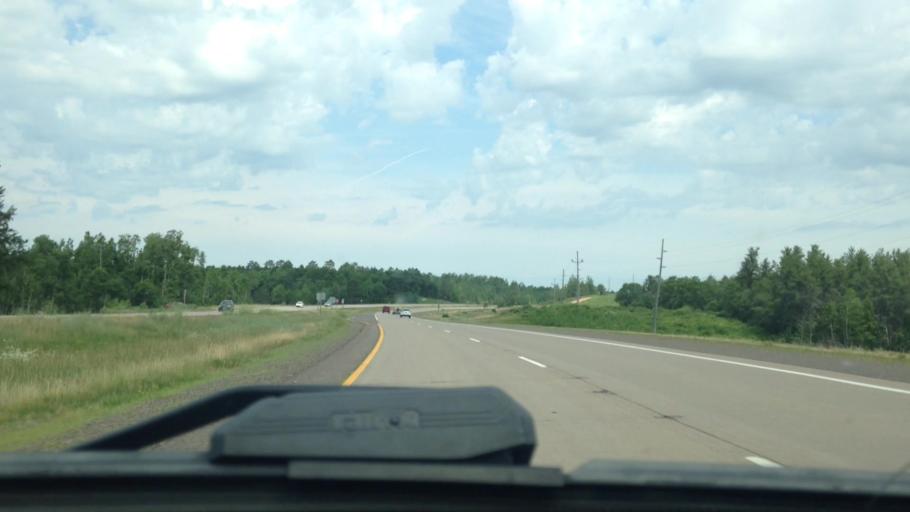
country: US
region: Wisconsin
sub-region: Douglas County
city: Lake Nebagamon
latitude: 46.2156
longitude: -91.7974
